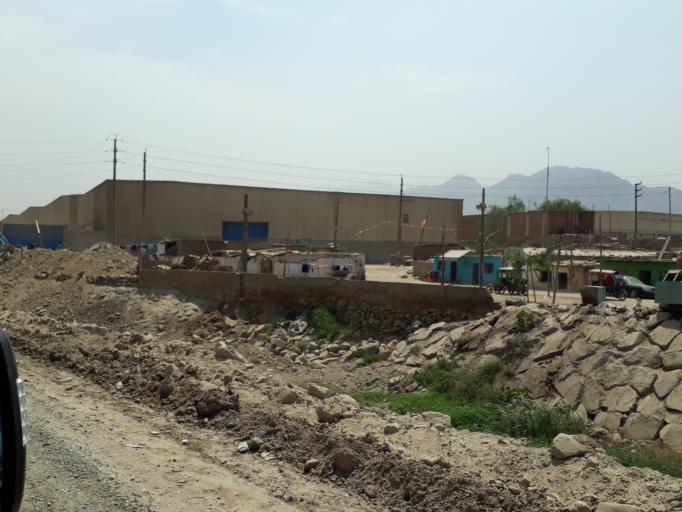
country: PE
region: Lima
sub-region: Lima
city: Santa Maria
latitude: -12.0002
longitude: -76.9163
